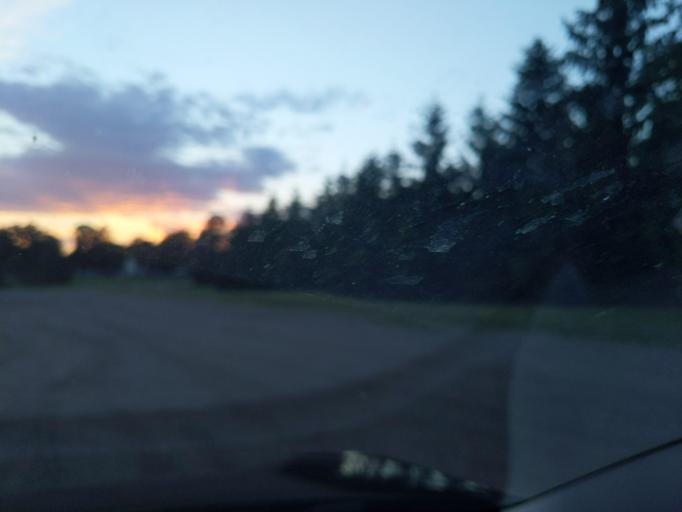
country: US
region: Michigan
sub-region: Eaton County
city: Eaton Rapids
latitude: 42.5118
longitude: -84.6595
